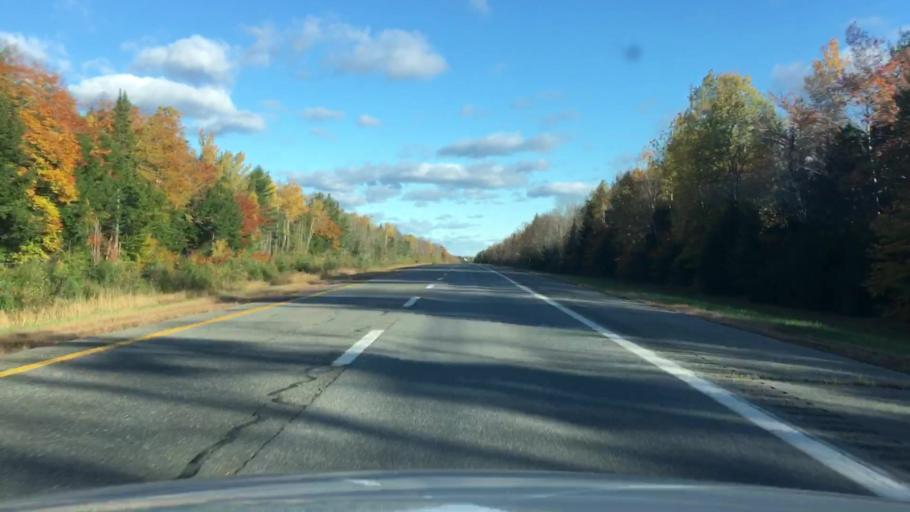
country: US
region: Maine
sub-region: Penobscot County
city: Greenbush
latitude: 45.0782
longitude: -68.6917
